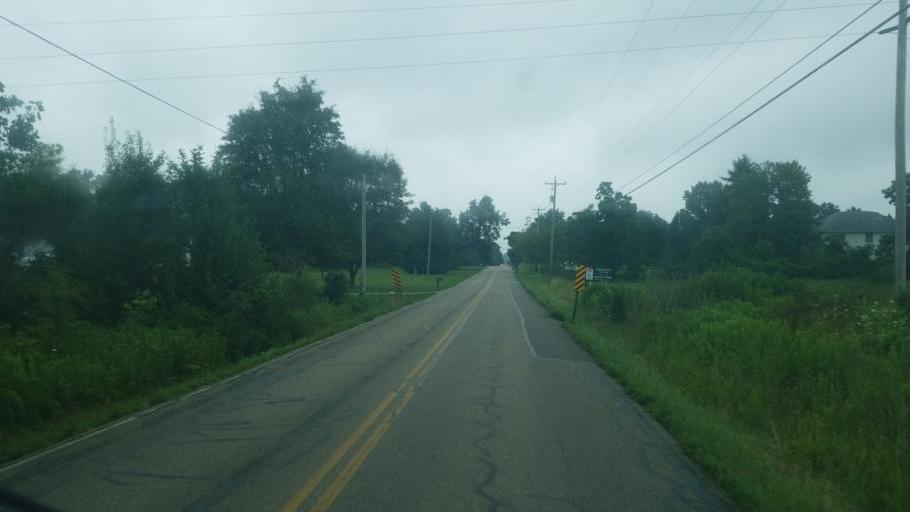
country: US
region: Ohio
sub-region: Delaware County
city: Sunbury
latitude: 40.2556
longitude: -82.9380
